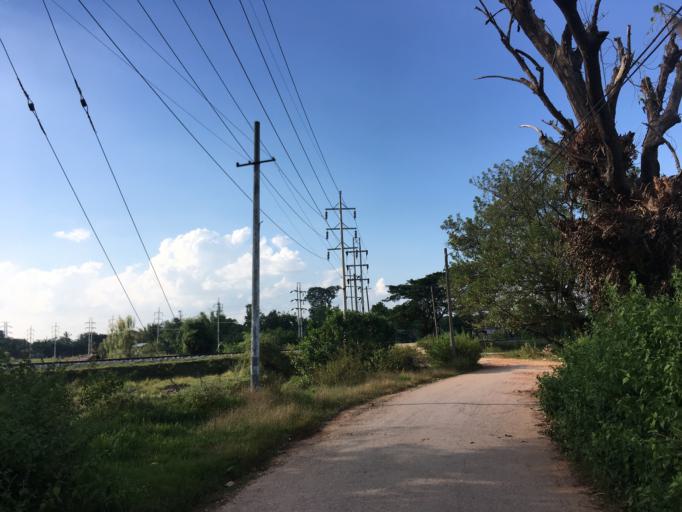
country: MM
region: Mon
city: Mawlamyine
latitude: 16.4304
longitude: 97.6220
